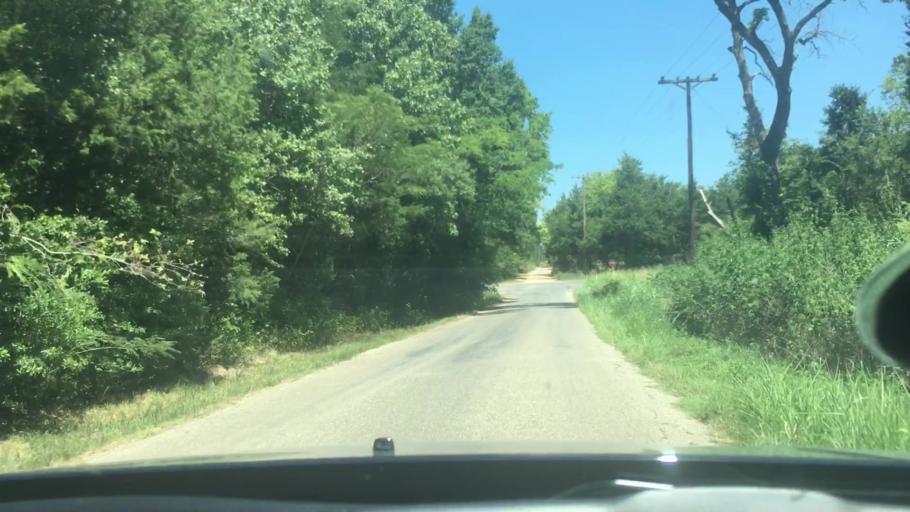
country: US
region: Oklahoma
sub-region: Bryan County
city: Durant
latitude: 33.9820
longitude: -96.2510
